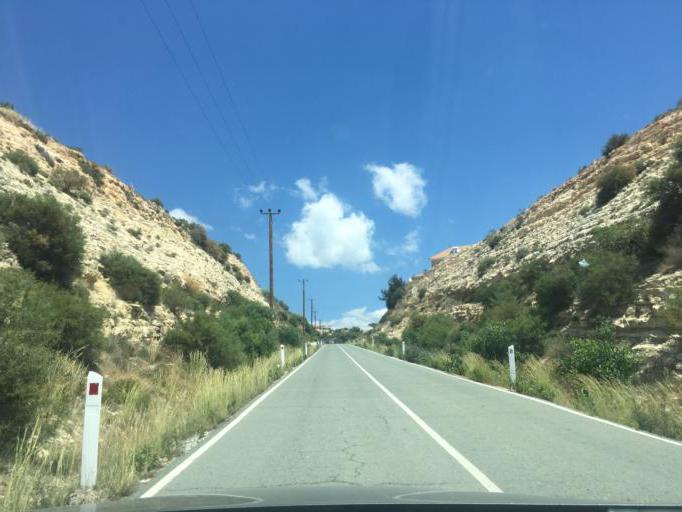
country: CY
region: Limassol
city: Mouttagiaka
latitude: 34.7498
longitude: 33.0566
